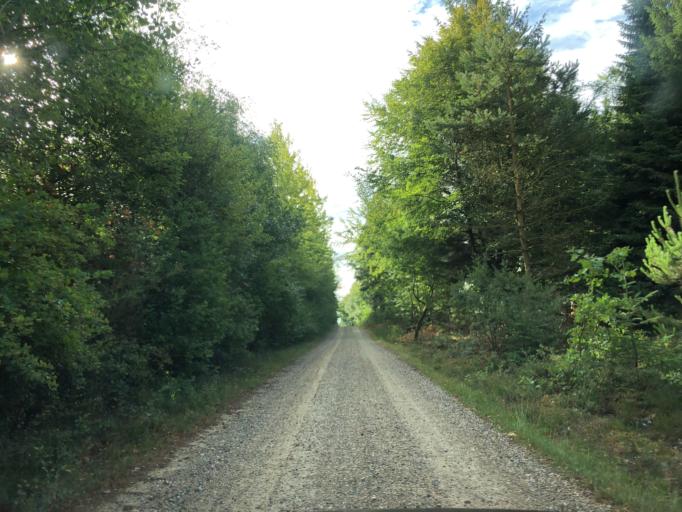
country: DK
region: Central Jutland
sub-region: Holstebro Kommune
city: Ulfborg
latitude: 56.1896
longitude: 8.3353
